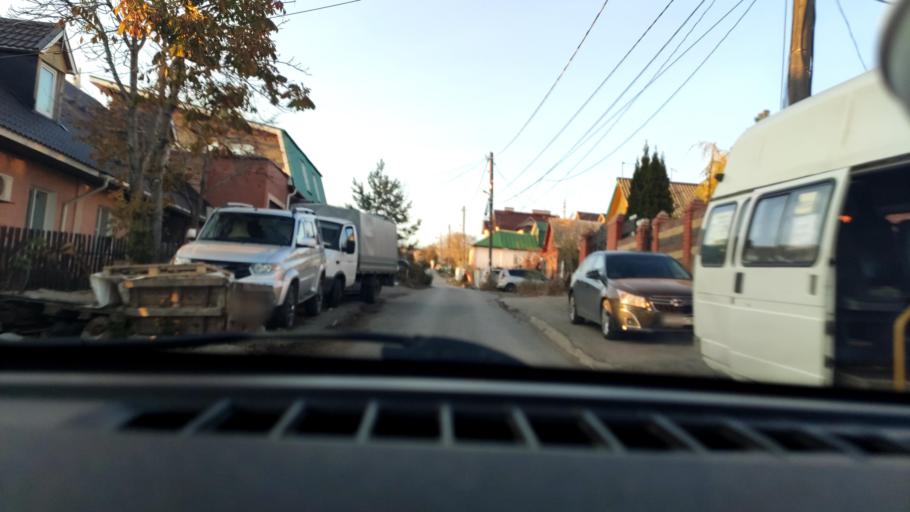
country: RU
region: Samara
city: Samara
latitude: 53.1845
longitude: 50.1857
